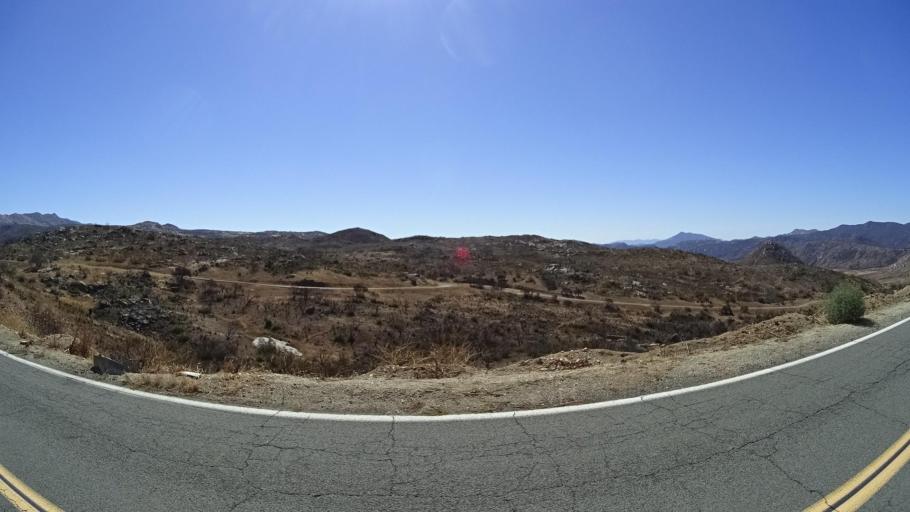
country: US
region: California
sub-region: San Diego County
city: Descanso
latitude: 32.7465
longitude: -116.6714
